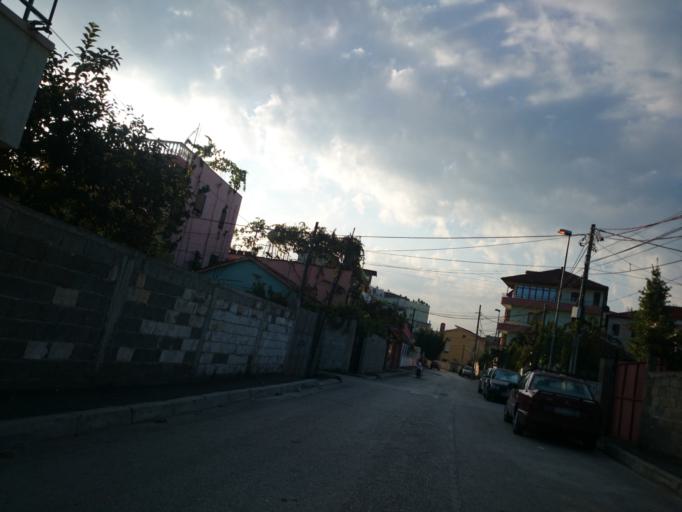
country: AL
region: Tirane
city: Tirana
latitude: 41.3292
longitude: 19.7916
